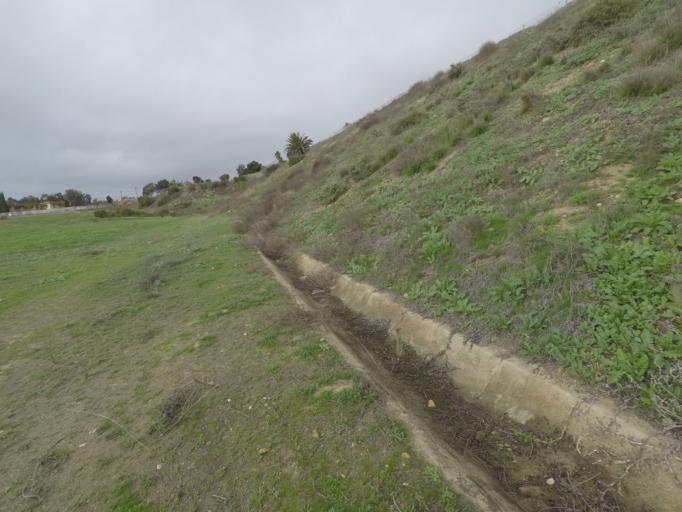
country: MX
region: Baja California
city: Tijuana
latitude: 32.5551
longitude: -117.0385
